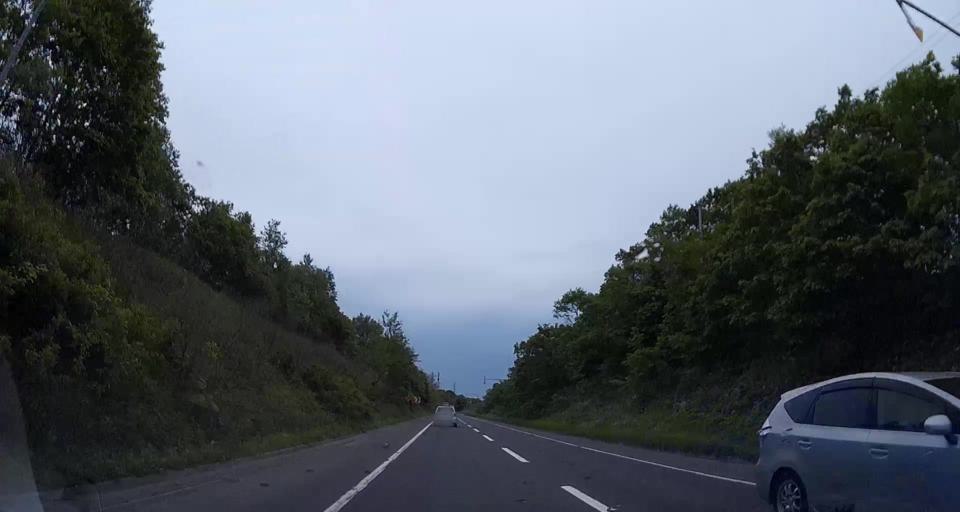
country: JP
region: Hokkaido
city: Chitose
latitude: 42.7015
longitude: 141.7424
